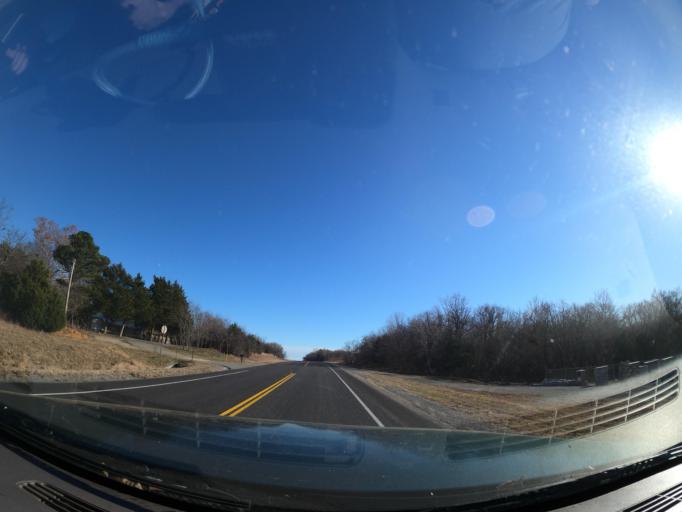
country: US
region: Oklahoma
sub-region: McIntosh County
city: Eufaula
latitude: 35.2538
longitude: -95.5752
